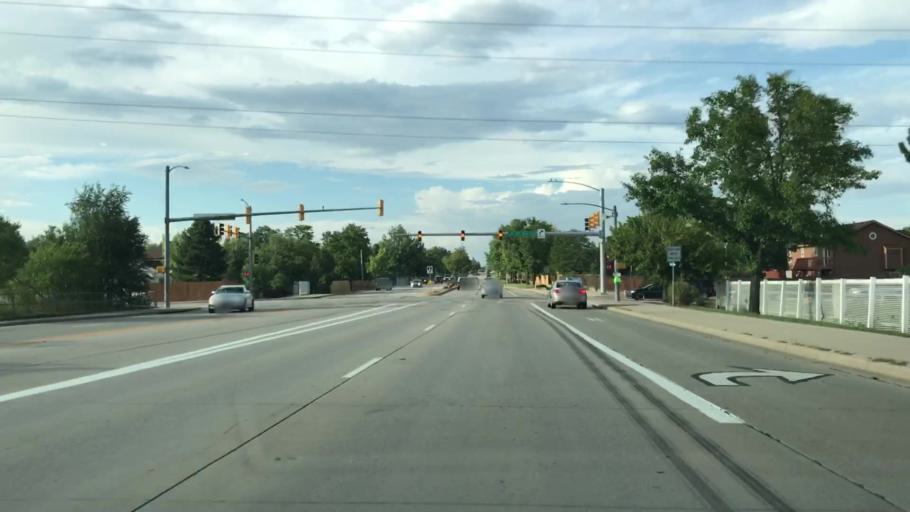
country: US
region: Colorado
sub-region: Boulder County
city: Longmont
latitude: 40.1955
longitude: -105.1308
